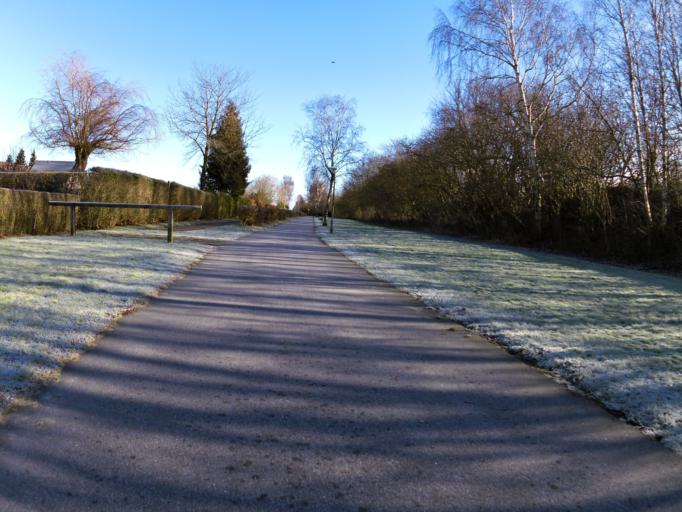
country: DK
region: Central Jutland
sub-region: Arhus Kommune
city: Kolt
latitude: 56.1019
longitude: 10.0659
